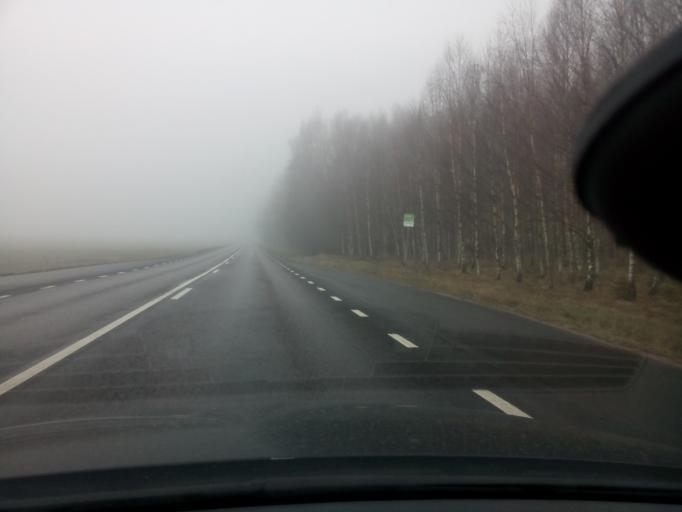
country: SE
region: Soedermanland
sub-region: Nykopings Kommun
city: Nykoping
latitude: 58.8101
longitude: 17.0808
